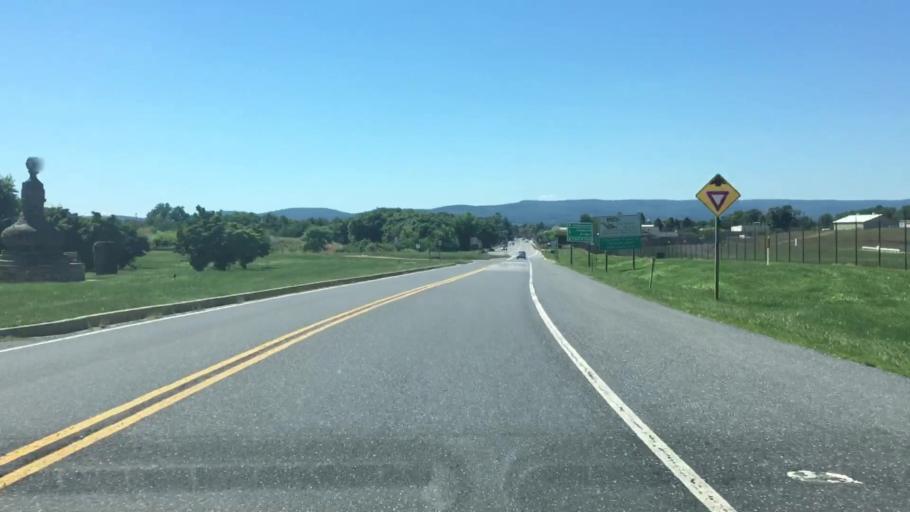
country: US
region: Maryland
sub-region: Frederick County
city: Bartonsville
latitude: 39.4048
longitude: -77.3827
